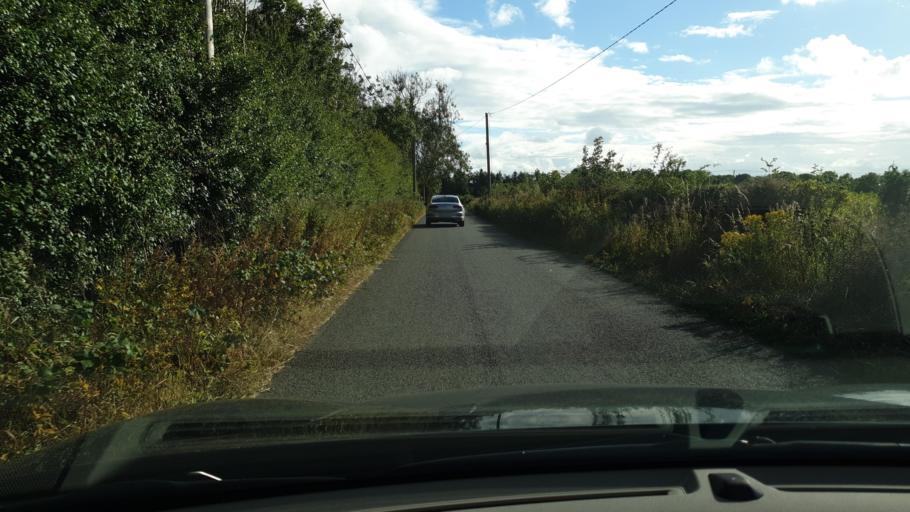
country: IE
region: Leinster
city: Hartstown
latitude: 53.4251
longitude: -6.4299
